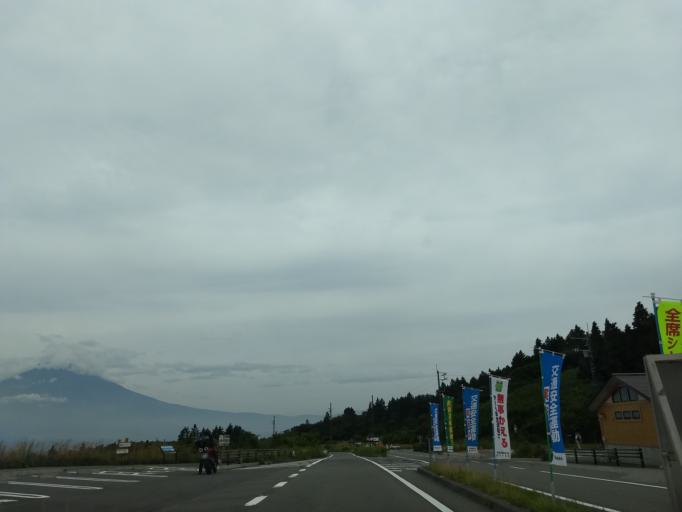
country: JP
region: Shizuoka
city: Gotemba
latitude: 35.2549
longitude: 138.9742
